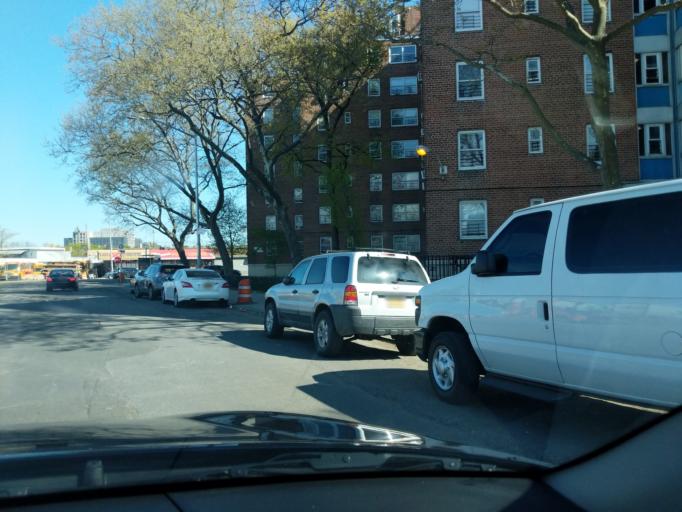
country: US
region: New York
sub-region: Kings County
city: East New York
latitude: 40.6529
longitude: -73.8969
